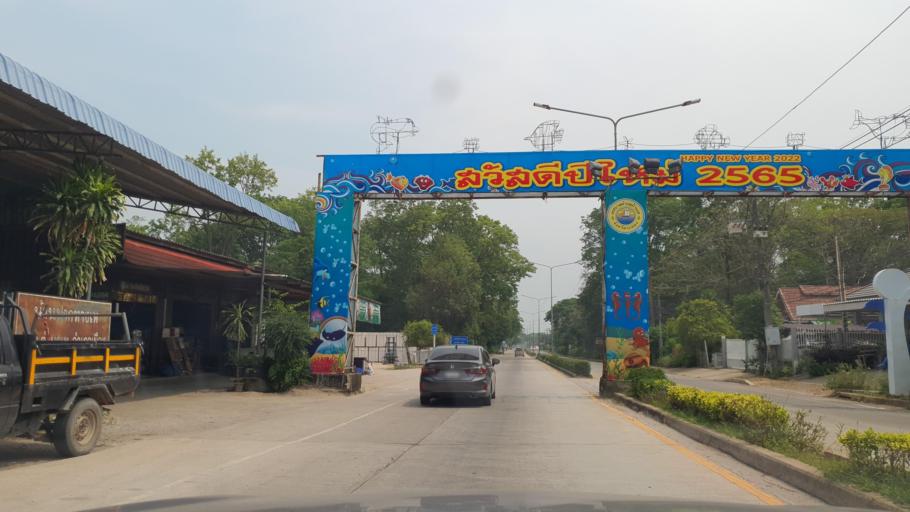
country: TH
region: Rayong
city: Rayong
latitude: 12.6415
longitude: 101.4222
